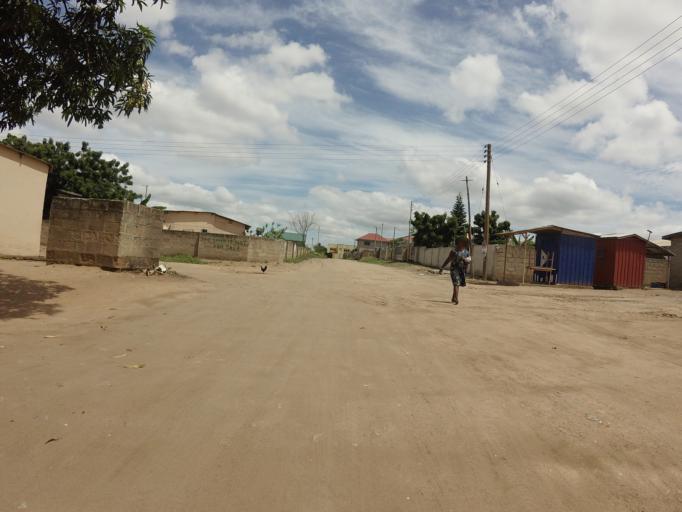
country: GH
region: Central
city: Kasoa
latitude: 5.5431
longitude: -0.4020
